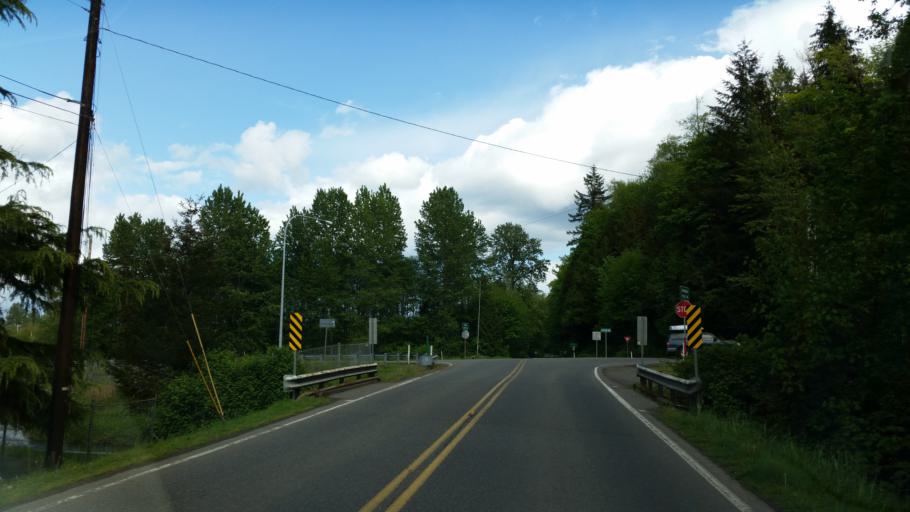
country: US
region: Washington
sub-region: Mason County
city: Shelton
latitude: 47.3011
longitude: -123.1821
